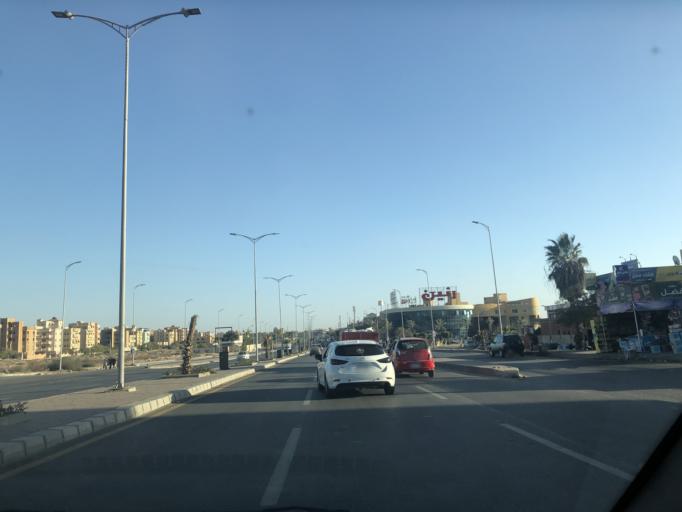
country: EG
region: Al Jizah
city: Madinat Sittah Uktubar
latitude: 29.9504
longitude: 30.9125
